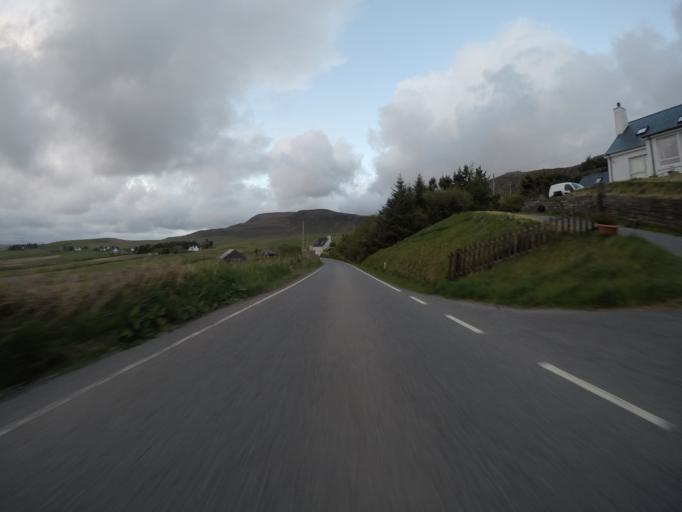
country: GB
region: Scotland
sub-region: Highland
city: Portree
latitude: 57.6118
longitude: -6.3721
